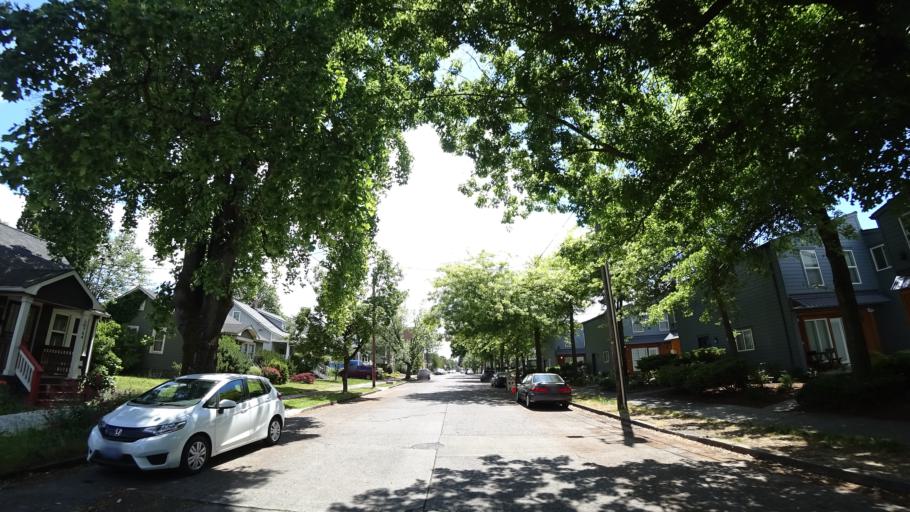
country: US
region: Oregon
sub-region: Multnomah County
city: Portland
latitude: 45.5650
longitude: -122.6760
